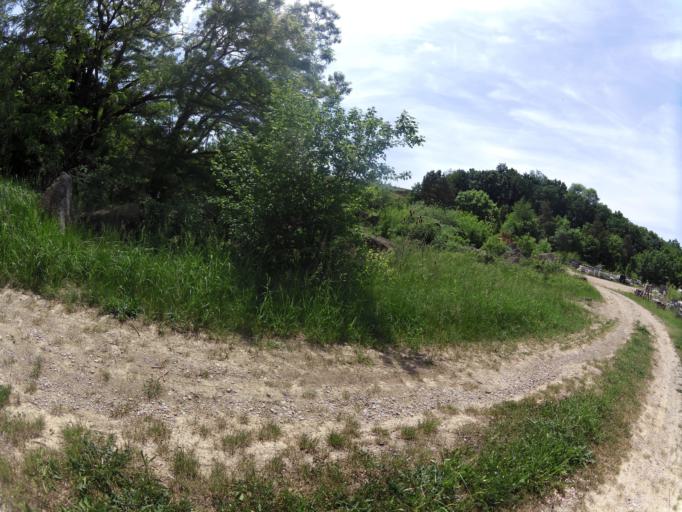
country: DE
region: Bavaria
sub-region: Regierungsbezirk Unterfranken
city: Sommerhausen
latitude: 49.6740
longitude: 10.0233
